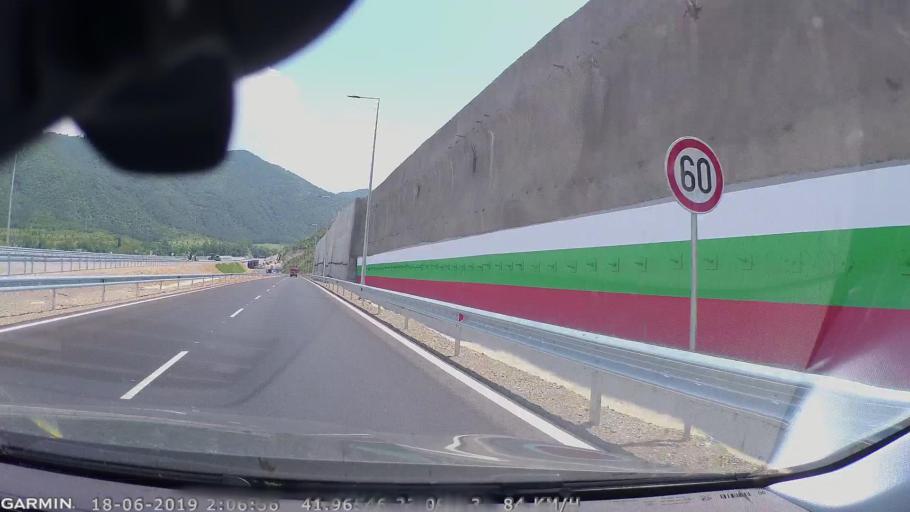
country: BG
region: Blagoevgrad
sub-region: Obshtina Blagoevgrad
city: Blagoevgrad
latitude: 41.9650
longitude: 23.0947
